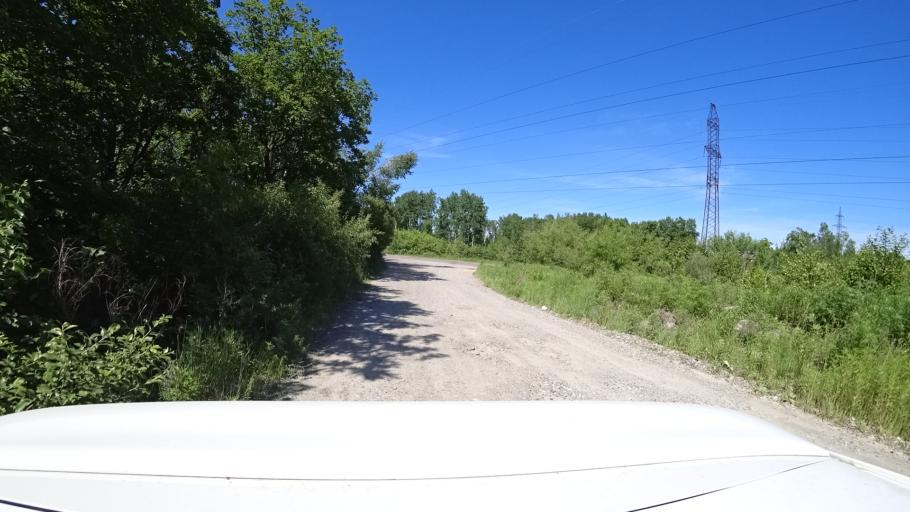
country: RU
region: Khabarovsk Krai
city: Topolevo
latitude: 48.5658
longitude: 135.1977
